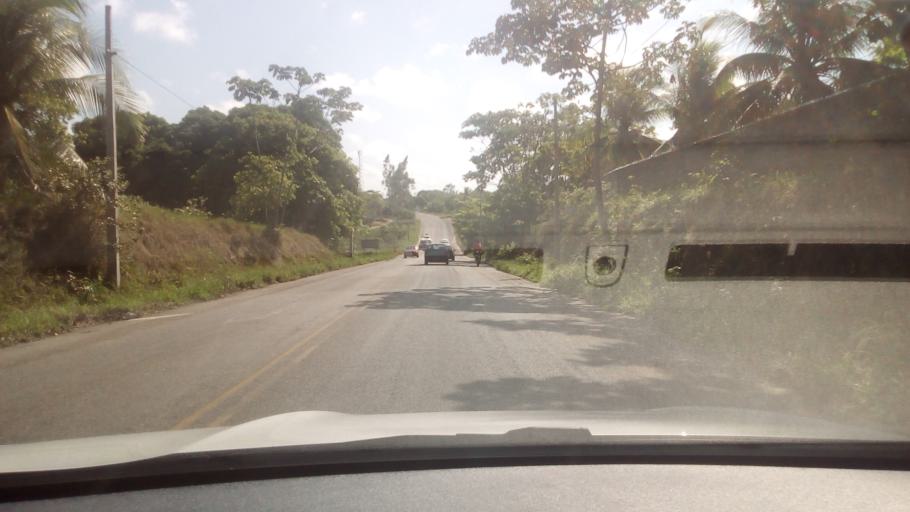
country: BR
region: Paraiba
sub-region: Conde
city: Conde
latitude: -7.2196
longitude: -34.8359
